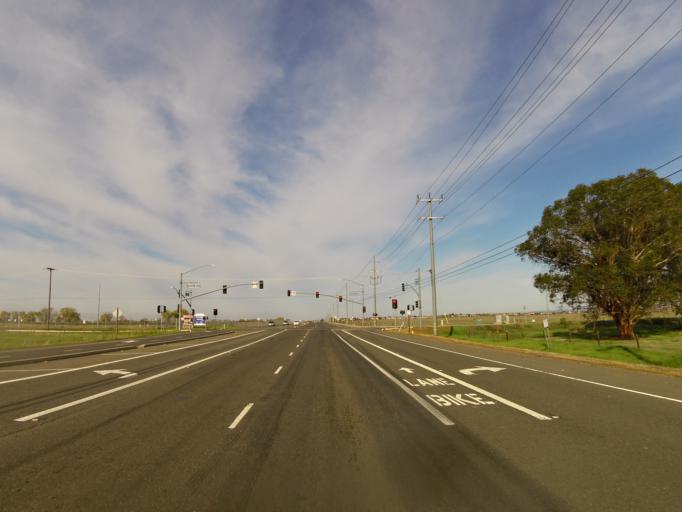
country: US
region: California
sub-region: Sacramento County
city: Rancho Cordova
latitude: 38.5247
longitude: -121.2428
